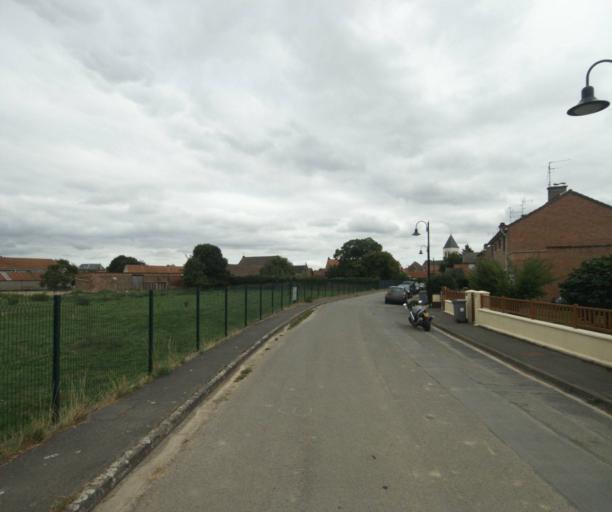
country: FR
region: Nord-Pas-de-Calais
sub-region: Departement du Nord
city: Sainghin-en-Melantois
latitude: 50.5690
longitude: 3.1653
